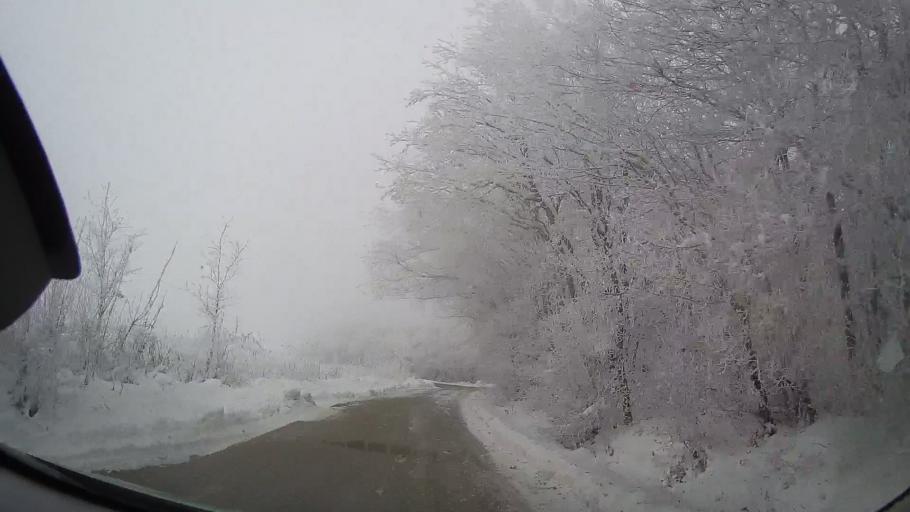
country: RO
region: Iasi
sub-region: Comuna Dagata
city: Dagata
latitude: 46.9154
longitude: 27.1817
